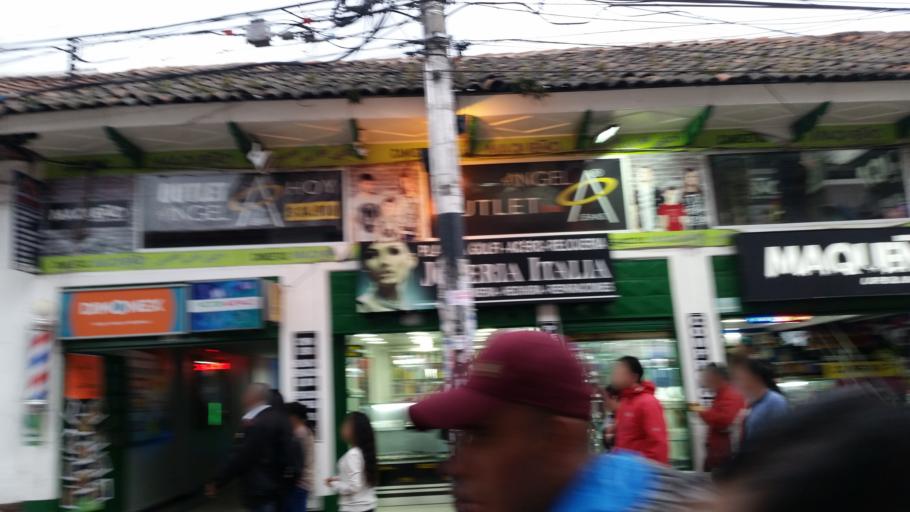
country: CO
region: Cundinamarca
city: Funza
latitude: 4.7158
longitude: -74.2128
